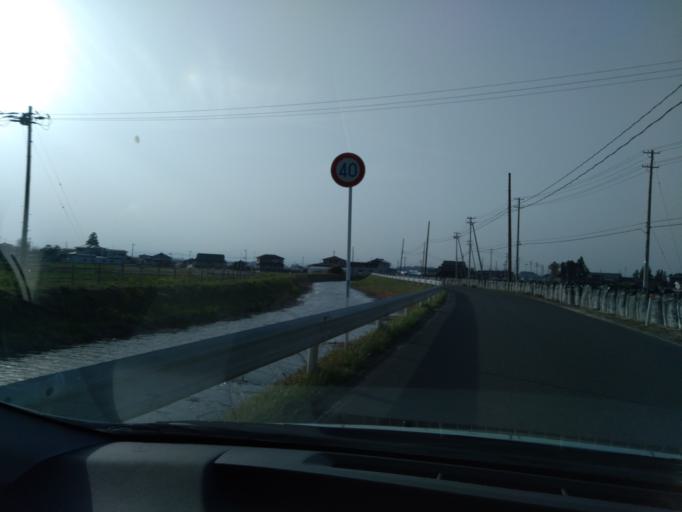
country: JP
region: Iwate
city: Ichinoseki
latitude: 38.7554
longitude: 141.1343
